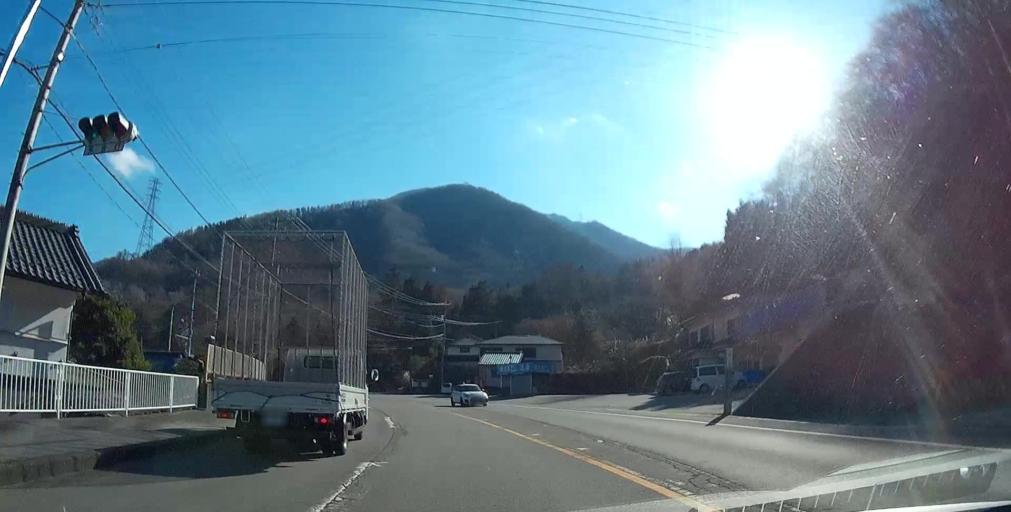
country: JP
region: Yamanashi
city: Fujikawaguchiko
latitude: 35.5759
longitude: 138.7636
